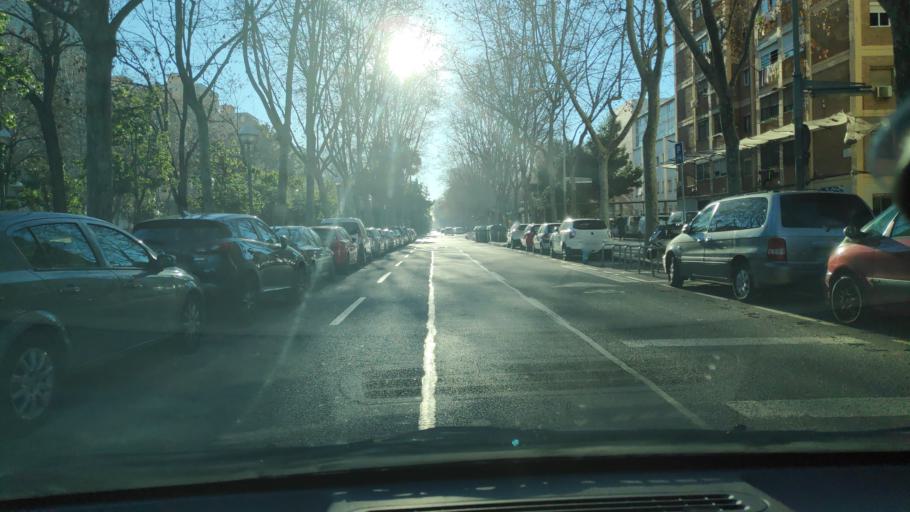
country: ES
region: Catalonia
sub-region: Provincia de Barcelona
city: Sant Marti
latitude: 41.4167
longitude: 2.2119
